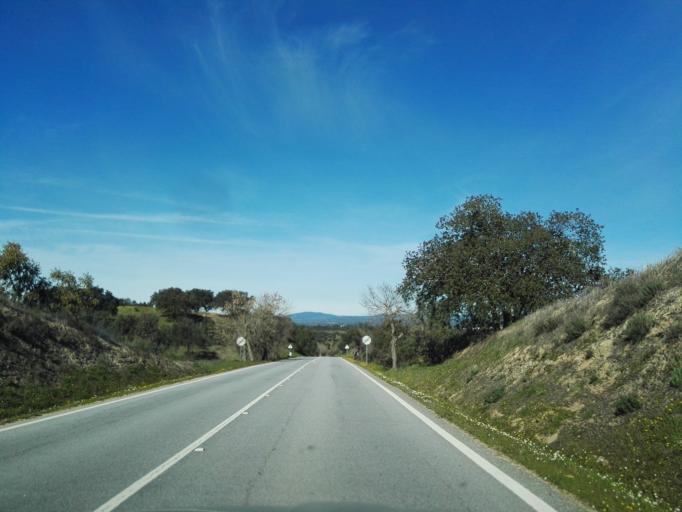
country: PT
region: Portalegre
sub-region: Arronches
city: Arronches
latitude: 39.0851
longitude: -7.2823
